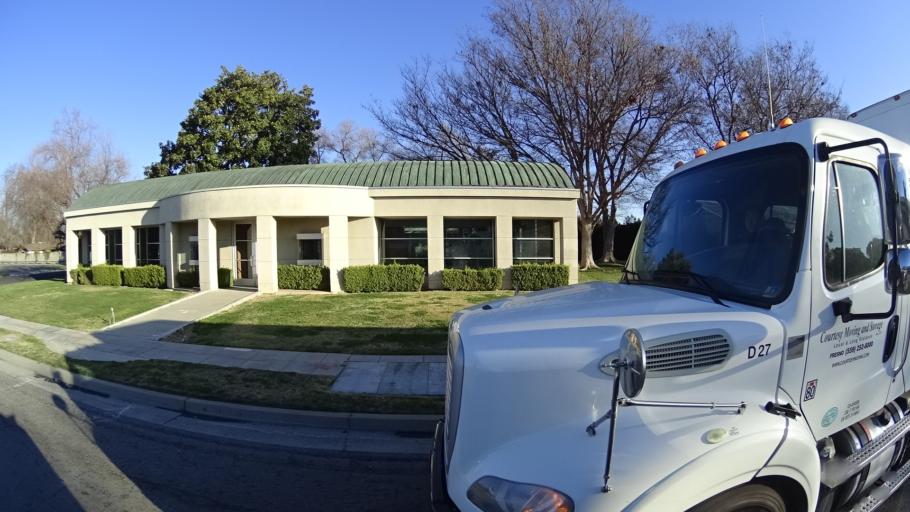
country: US
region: California
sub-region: Fresno County
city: Fresno
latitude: 36.8085
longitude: -119.7968
